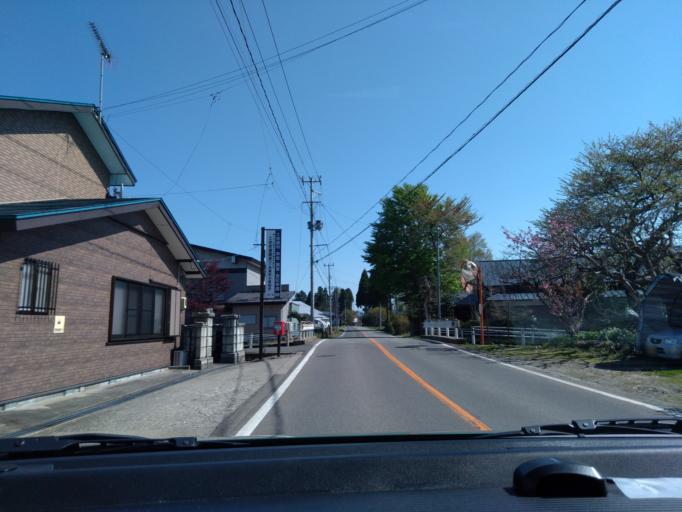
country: JP
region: Akita
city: Kakunodatemachi
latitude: 39.5675
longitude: 140.5828
